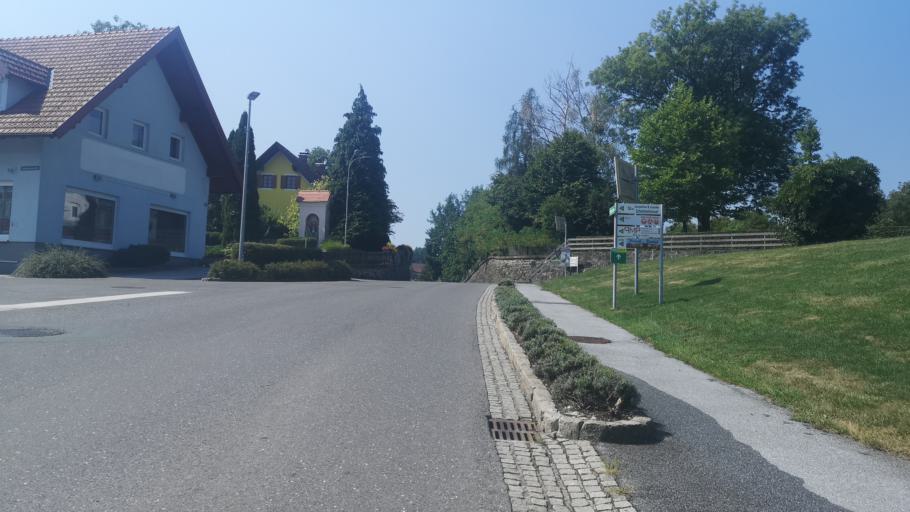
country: AT
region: Styria
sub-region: Politischer Bezirk Deutschlandsberg
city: Lannach
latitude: 46.9449
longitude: 15.3344
